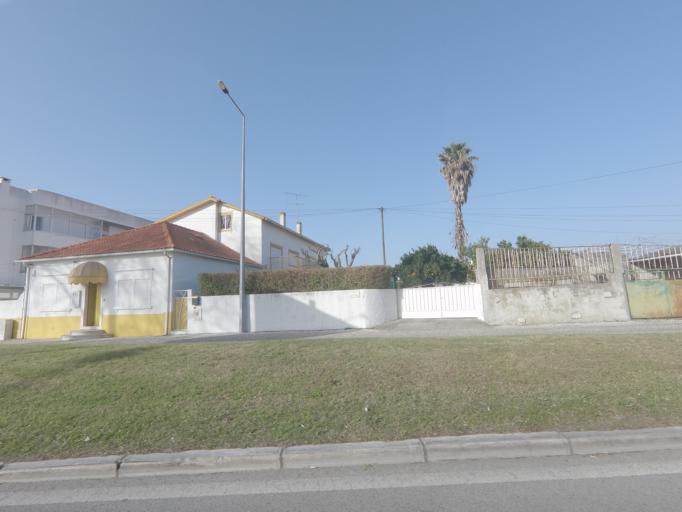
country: PT
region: Leiria
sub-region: Marinha Grande
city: Marinha Grande
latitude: 39.7496
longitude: -8.9214
